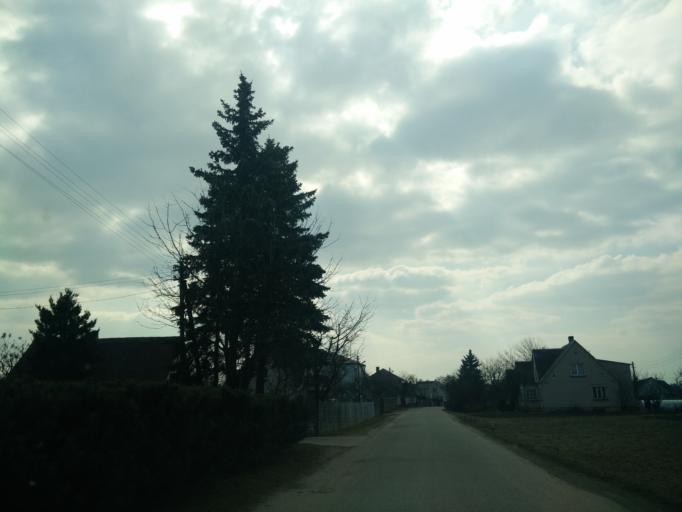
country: LT
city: Trakai
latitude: 54.6103
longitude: 24.9866
